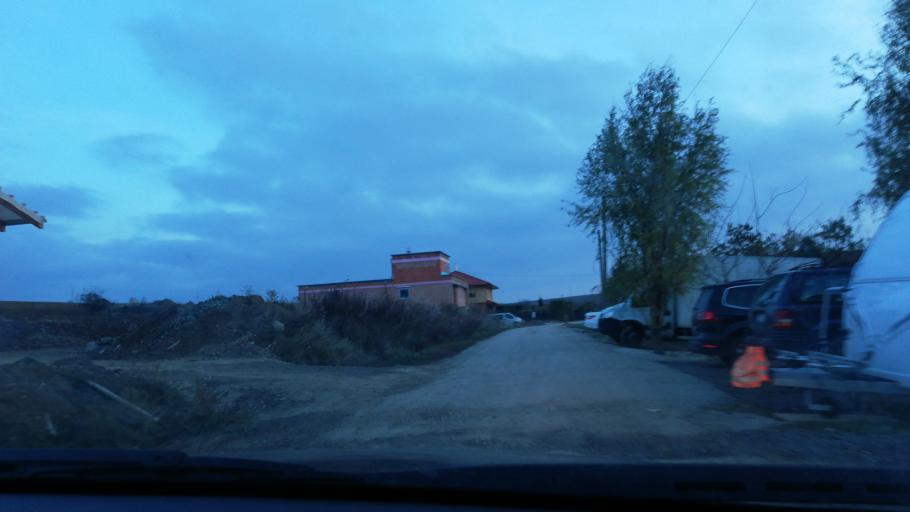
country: SK
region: Nitriansky
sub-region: Okres Nitra
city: Nitra
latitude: 48.3166
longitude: 17.9949
